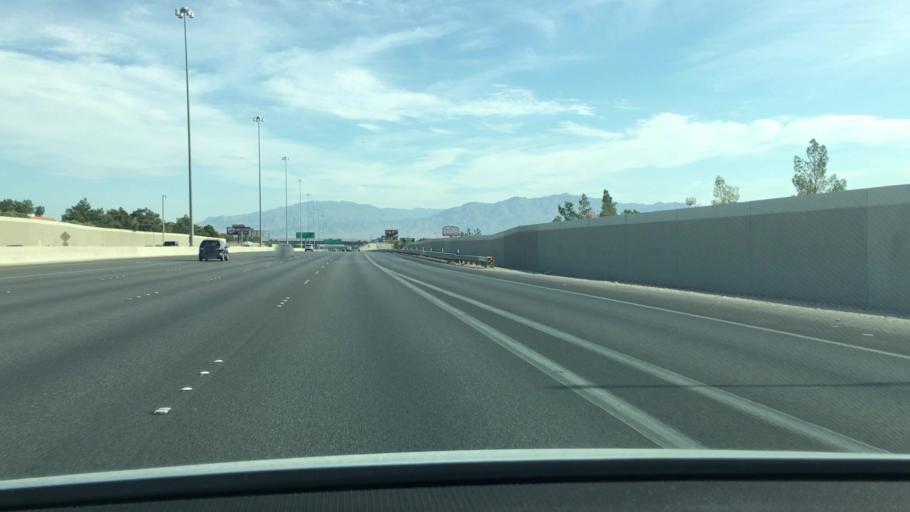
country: US
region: Nevada
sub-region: Clark County
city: Spring Valley
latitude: 36.1831
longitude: -115.2443
